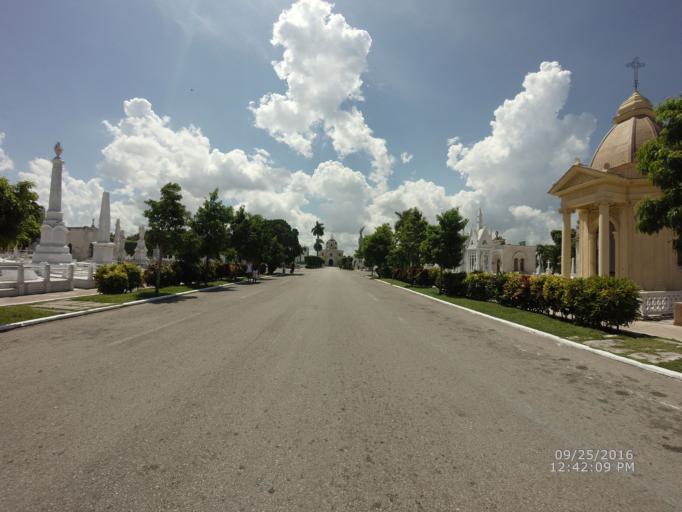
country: CU
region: La Habana
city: Havana
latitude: 23.1253
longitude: -82.3987
